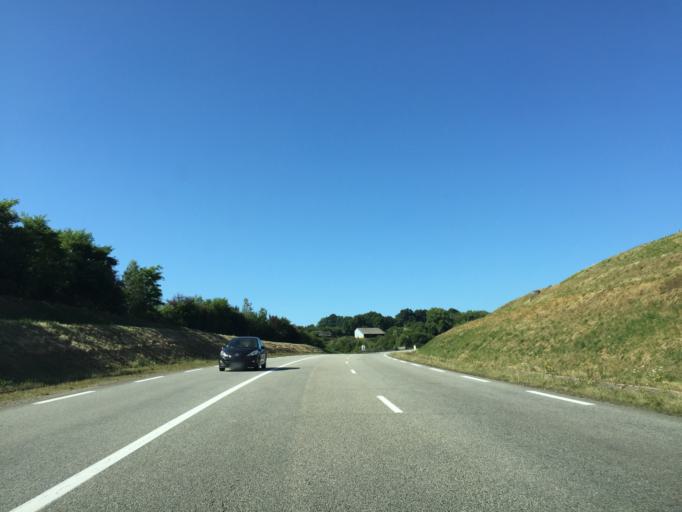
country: FR
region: Lower Normandy
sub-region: Departement du Calvados
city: Lisieux
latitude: 49.1816
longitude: 0.2272
